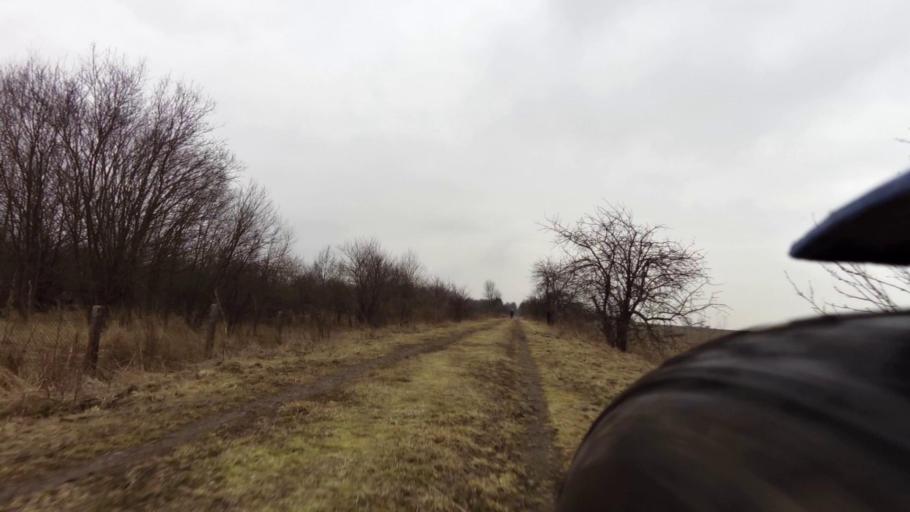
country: PL
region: West Pomeranian Voivodeship
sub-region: Powiat walecki
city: Walcz
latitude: 53.2545
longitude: 16.4791
